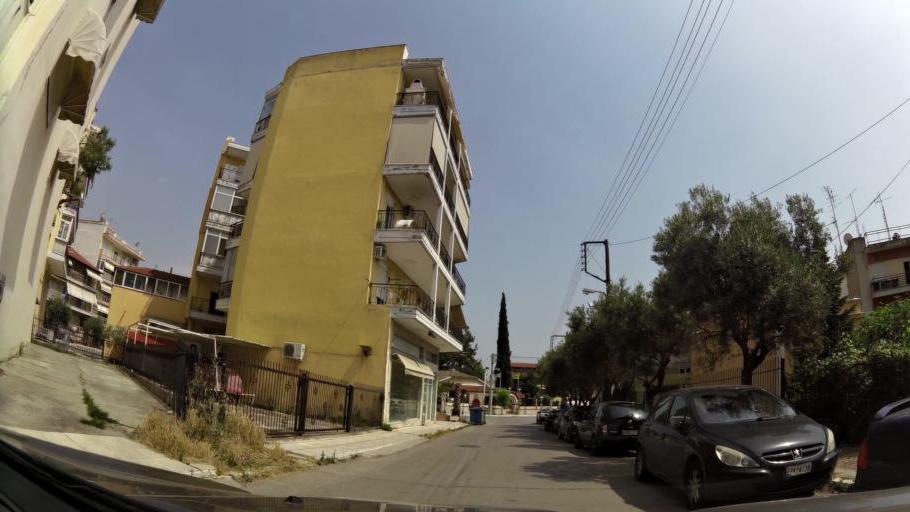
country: GR
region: Central Macedonia
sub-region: Nomos Thessalonikis
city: Diavata
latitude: 40.6889
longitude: 22.8585
